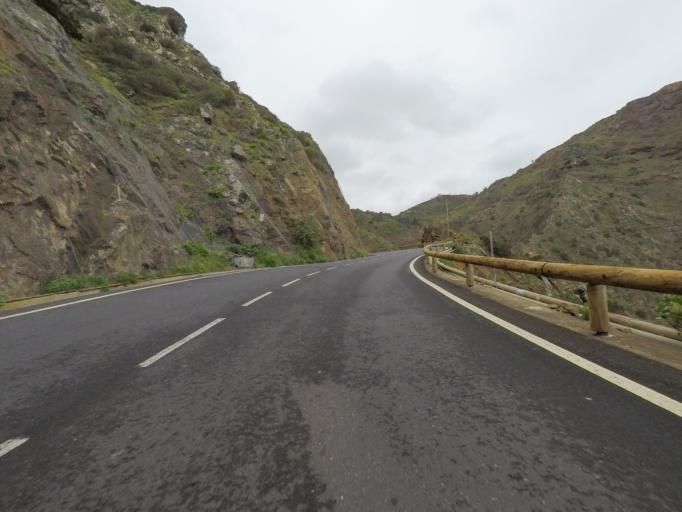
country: ES
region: Canary Islands
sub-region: Provincia de Santa Cruz de Tenerife
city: Agulo
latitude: 28.1884
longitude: -17.2092
